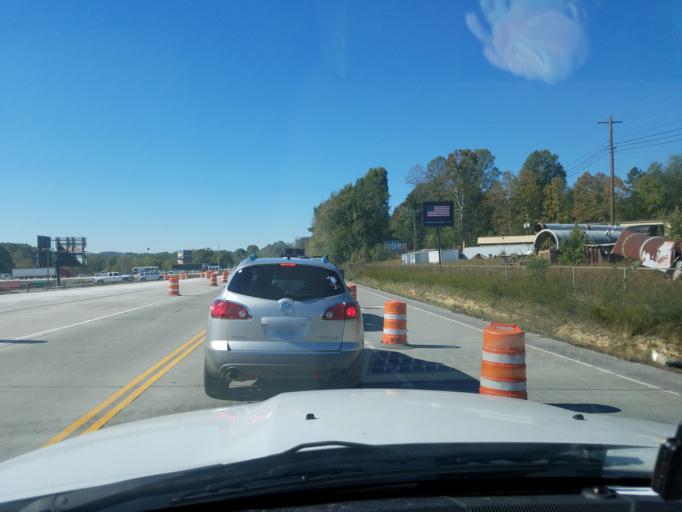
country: US
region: Kentucky
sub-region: Laurel County
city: North Corbin
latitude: 36.9681
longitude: -84.0827
